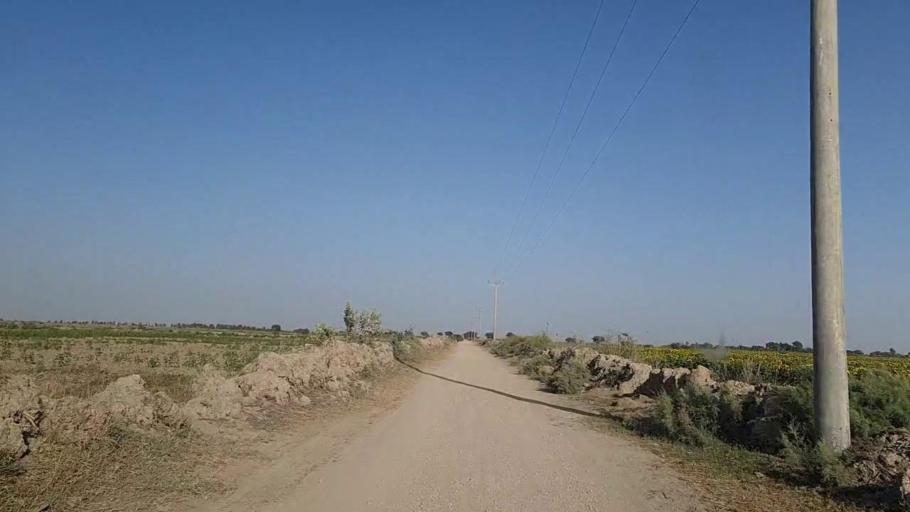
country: PK
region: Sindh
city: Jati
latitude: 24.4227
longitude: 68.2791
